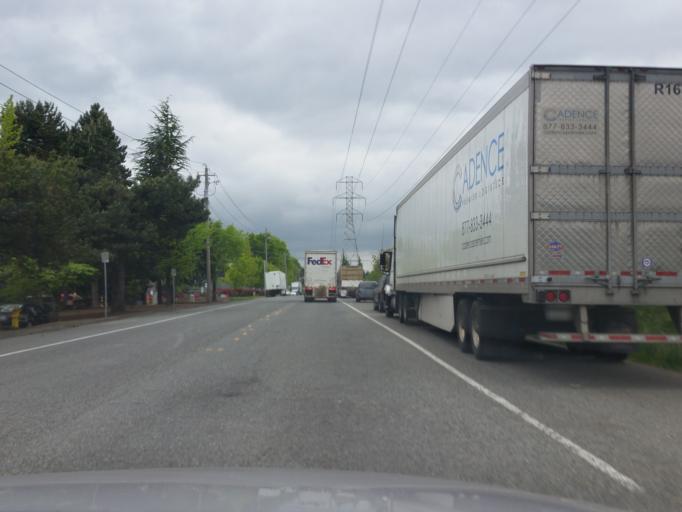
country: US
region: Washington
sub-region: King County
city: Bellevue
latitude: 47.6242
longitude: -122.1751
